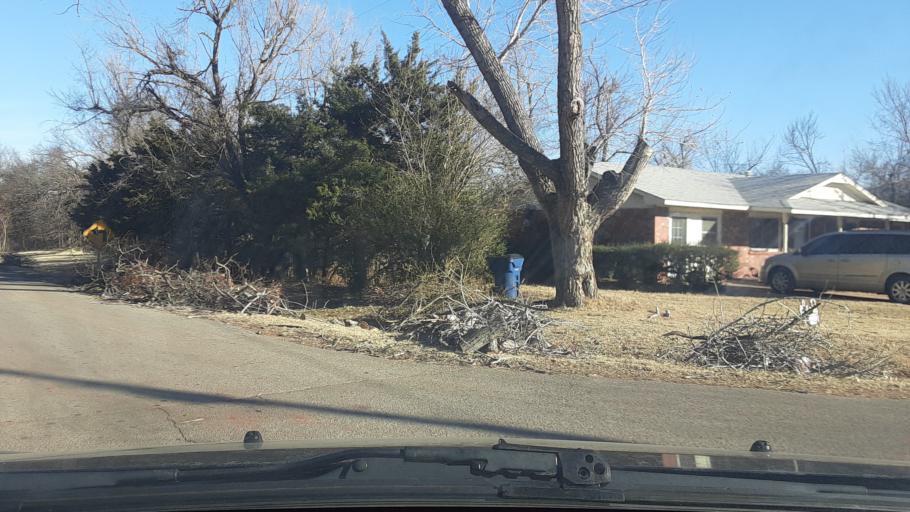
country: US
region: Oklahoma
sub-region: Logan County
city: Guthrie
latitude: 35.8760
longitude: -97.4026
